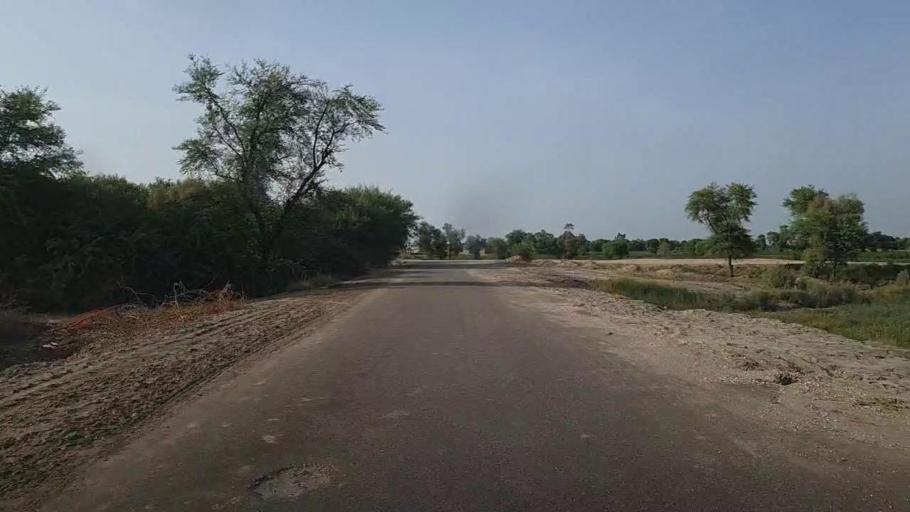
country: PK
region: Sindh
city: Ubauro
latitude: 28.0998
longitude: 69.8455
